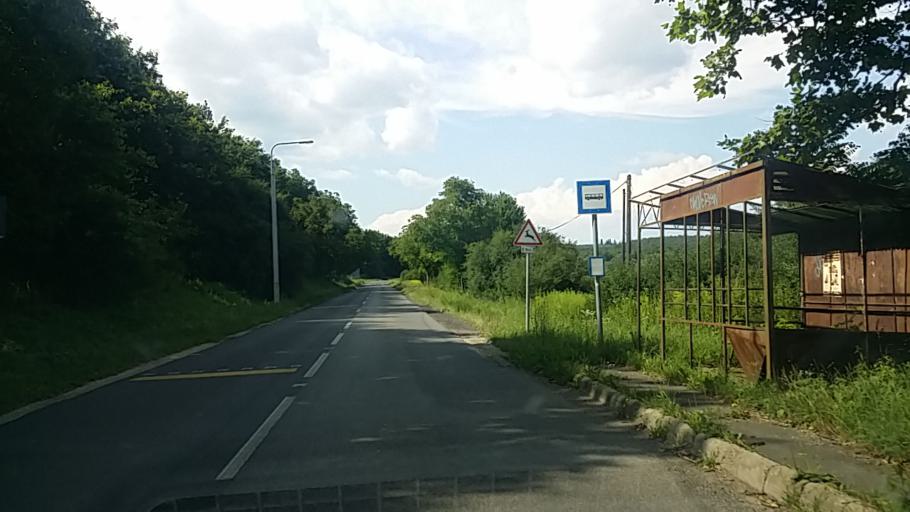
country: HU
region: Zala
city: Becsehely
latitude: 46.4532
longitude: 16.8119
